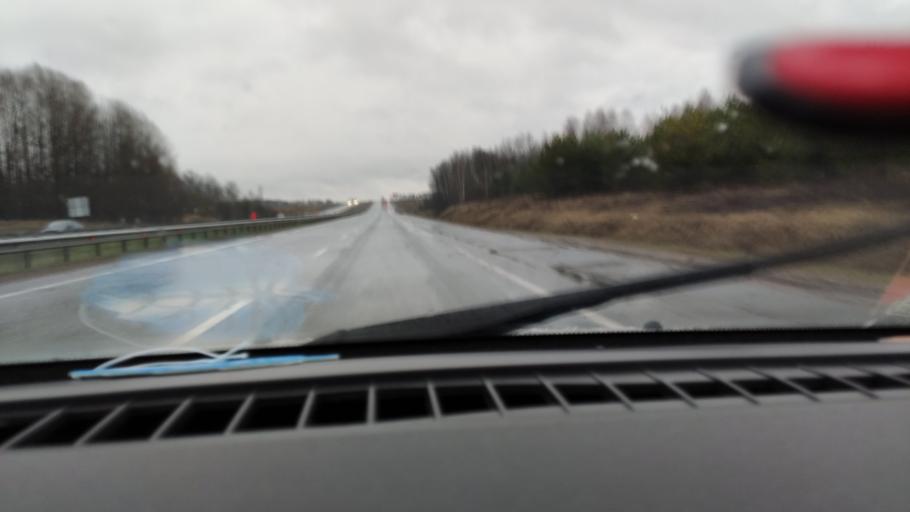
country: RU
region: Tatarstan
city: Yelabuga
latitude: 55.7930
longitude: 52.1573
